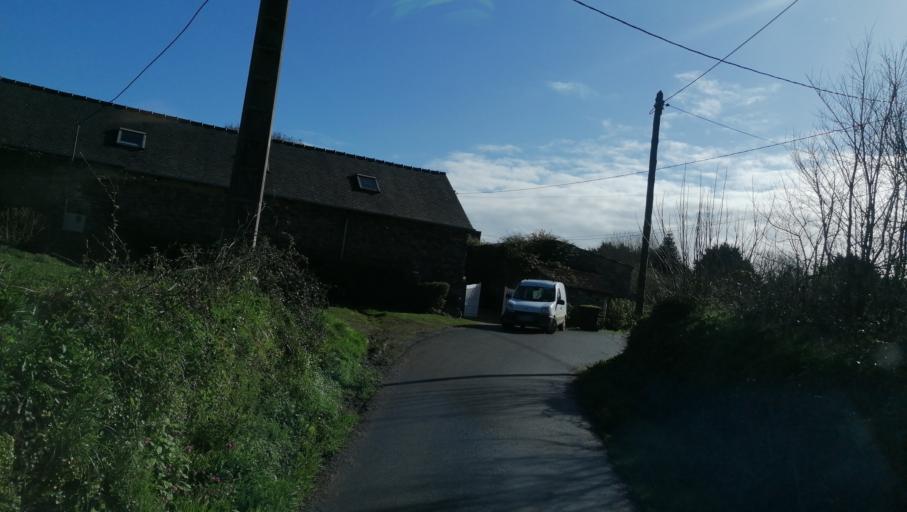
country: FR
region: Brittany
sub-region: Departement des Cotes-d'Armor
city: Plouha
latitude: 48.6589
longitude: -2.9289
